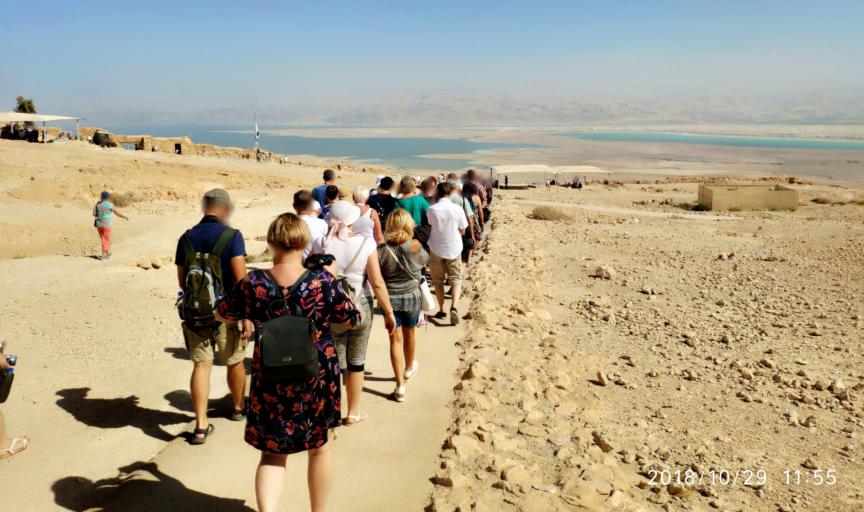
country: IL
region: Southern District
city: `En Boqeq
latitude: 31.3159
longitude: 35.3537
